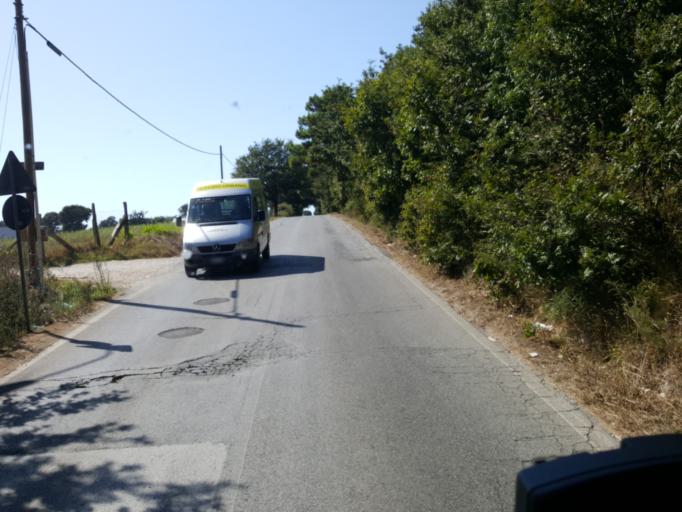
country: IT
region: Latium
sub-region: Citta metropolitana di Roma Capitale
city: Nettuno
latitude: 41.5128
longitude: 12.6445
